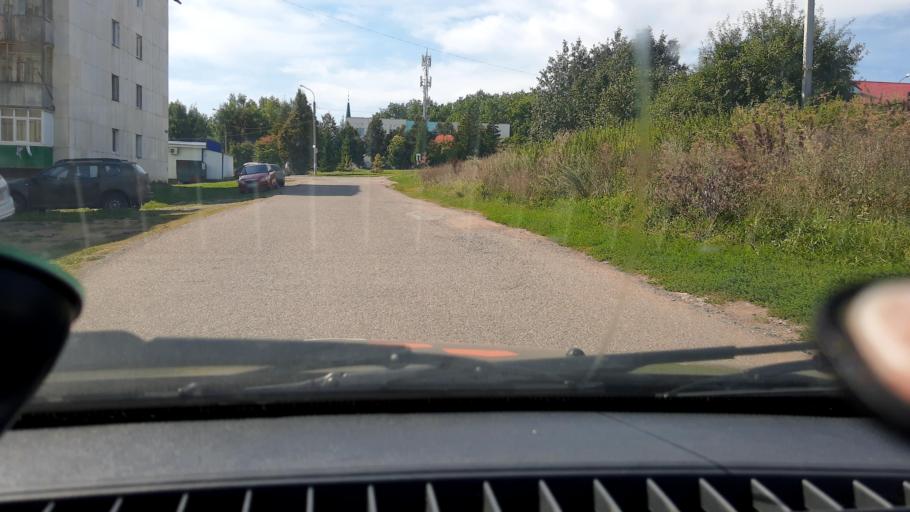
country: RU
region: Bashkortostan
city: Avdon
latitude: 54.6707
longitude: 55.7164
